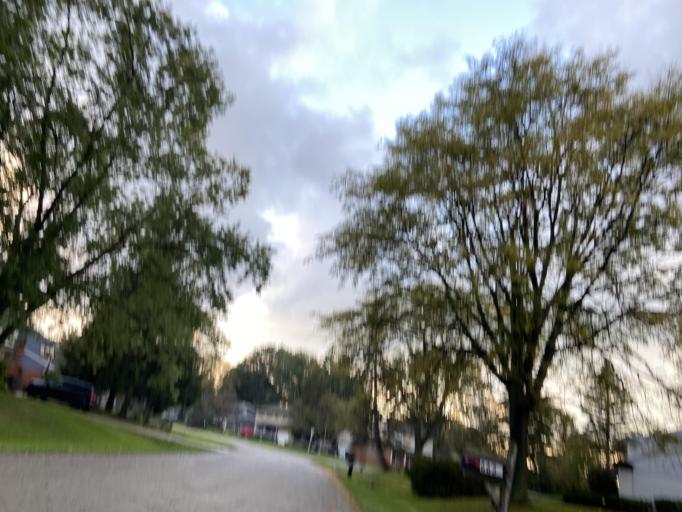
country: US
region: Michigan
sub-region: Oakland County
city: West Bloomfield Township
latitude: 42.5412
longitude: -83.3573
